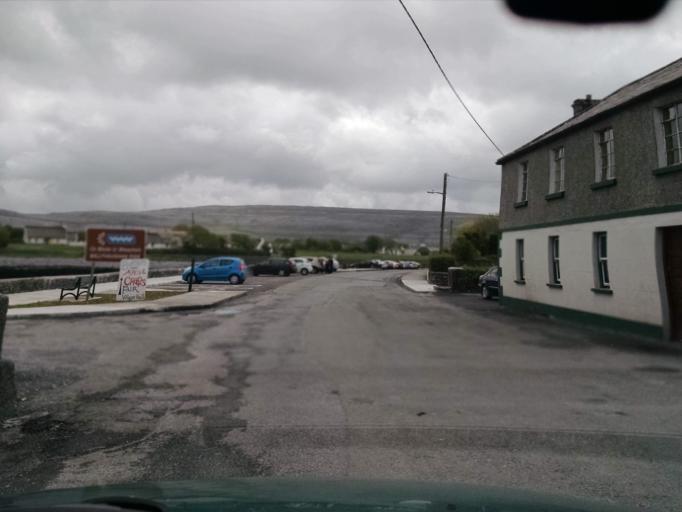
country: IE
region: Connaught
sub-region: County Galway
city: Bearna
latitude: 53.1198
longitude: -9.1541
